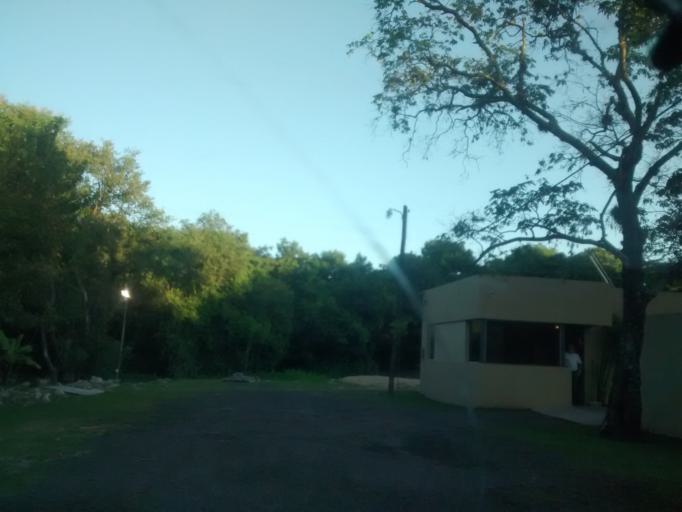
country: AR
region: Chaco
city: Fontana
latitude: -27.4189
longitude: -59.0085
